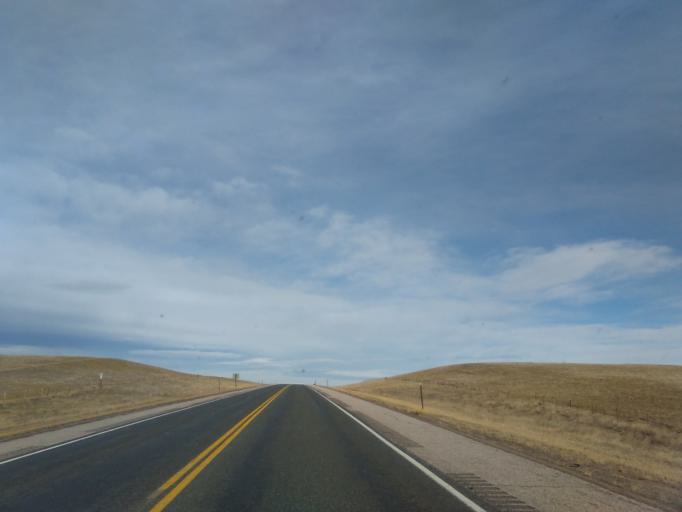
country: US
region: Wyoming
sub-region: Laramie County
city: Pine Bluffs
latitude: 41.5936
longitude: -104.2660
